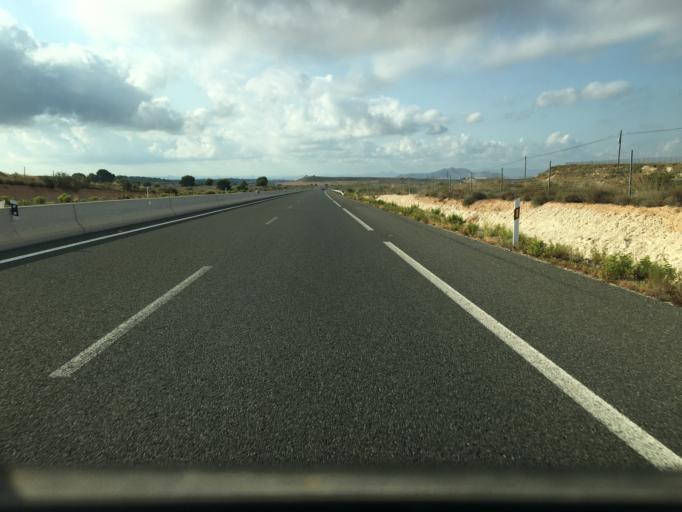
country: ES
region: Murcia
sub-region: Murcia
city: Beniel
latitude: 37.9127
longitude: -0.9591
